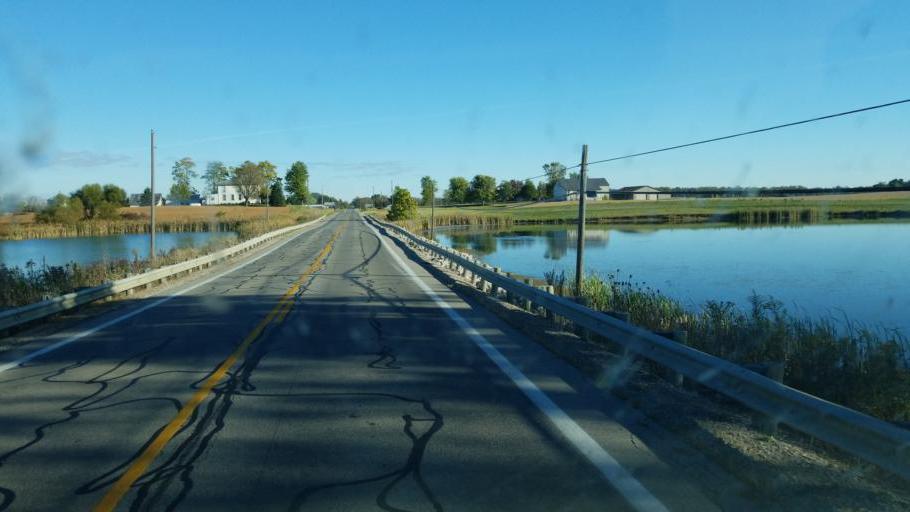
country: US
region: Ohio
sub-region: Morrow County
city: Mount Gilead
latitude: 40.5989
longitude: -82.8236
